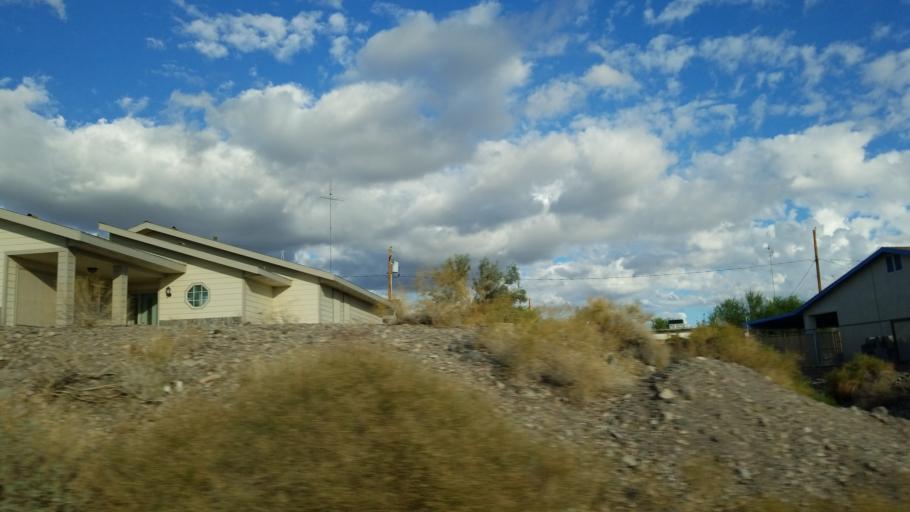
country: US
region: Arizona
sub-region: Mohave County
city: Lake Havasu City
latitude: 34.4652
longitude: -114.2609
